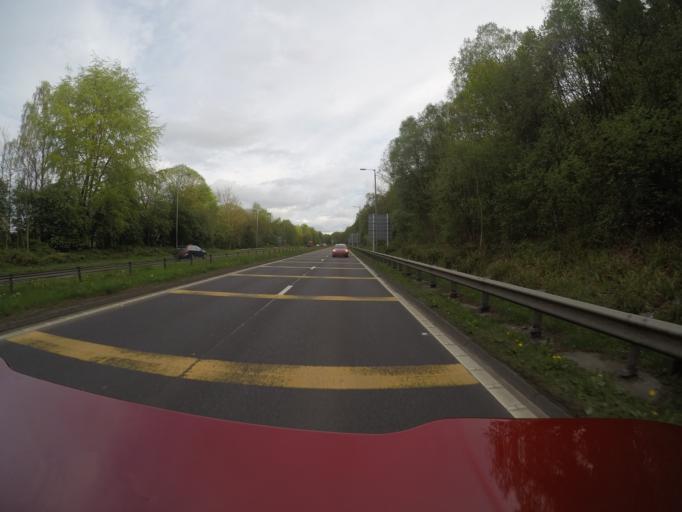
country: GB
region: Scotland
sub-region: West Dunbartonshire
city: Alexandria
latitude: 55.9957
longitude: -4.5958
